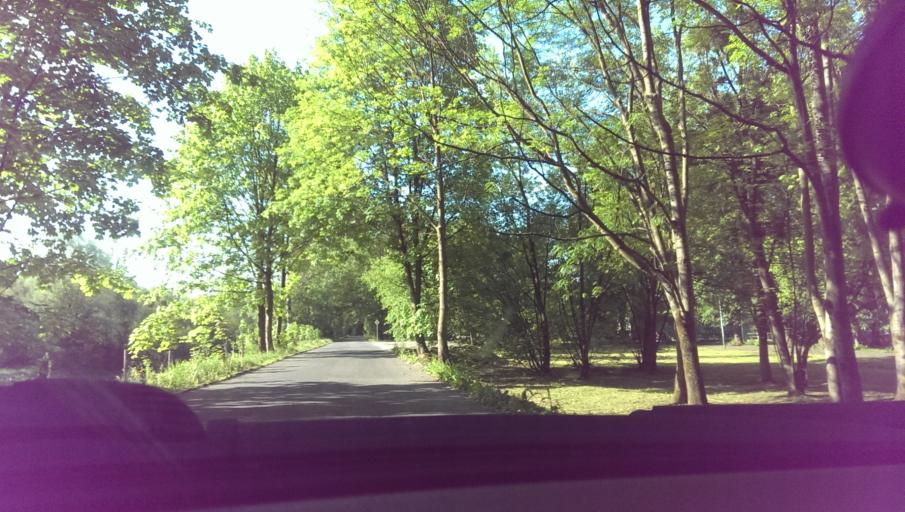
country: CZ
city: Frydlant nad Ostravici
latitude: 49.5826
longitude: 18.3650
